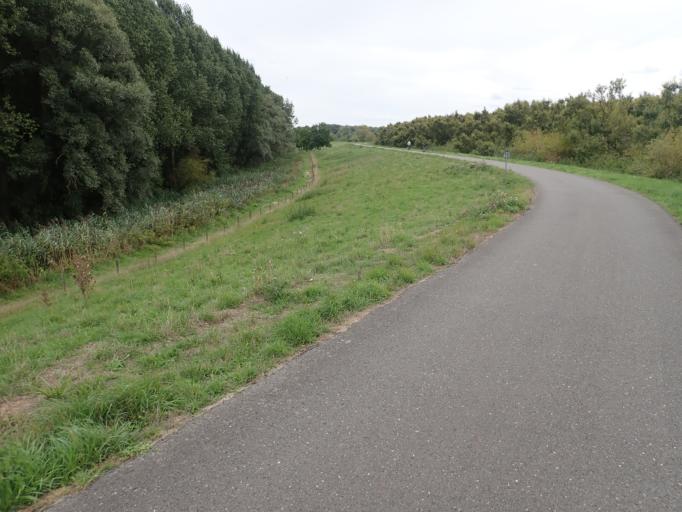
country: BE
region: Flanders
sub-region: Provincie Oost-Vlaanderen
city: Hamme
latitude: 51.0911
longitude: 4.1750
